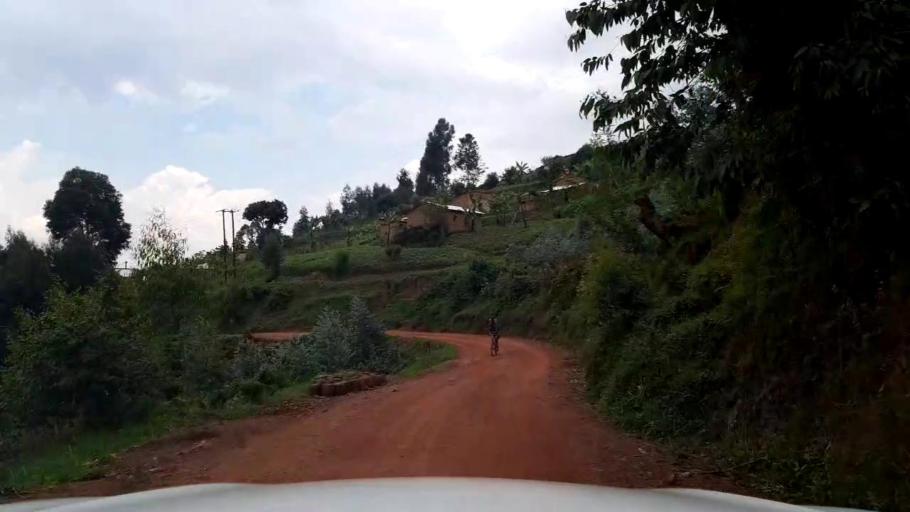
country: RW
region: Northern Province
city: Byumba
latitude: -1.5252
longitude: 29.9536
